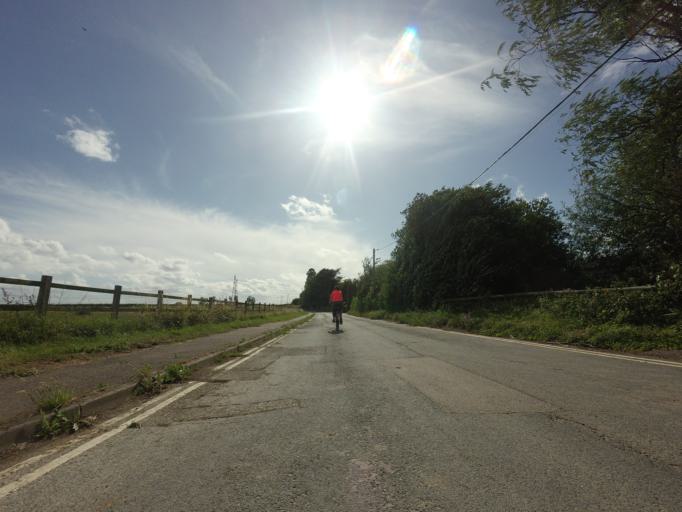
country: GB
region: England
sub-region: Kent
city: Hoo
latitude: 51.4307
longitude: 0.5878
